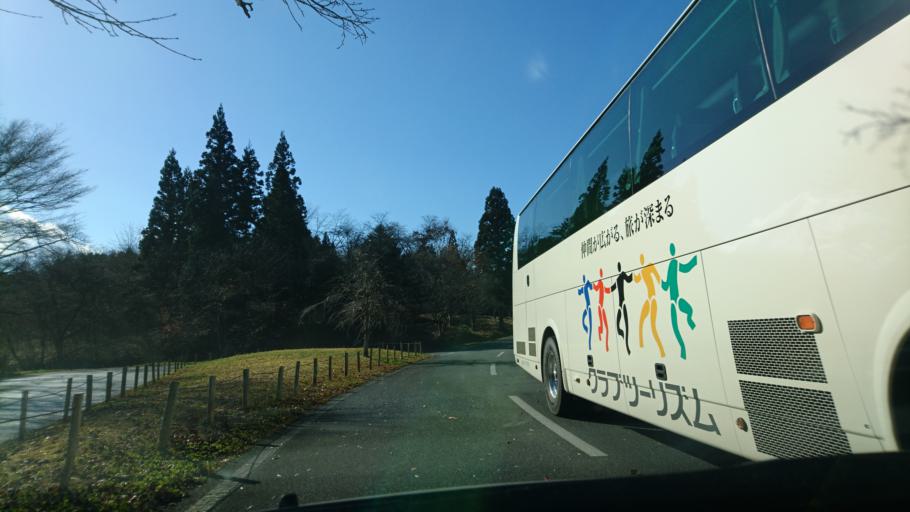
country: JP
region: Iwate
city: Ichinoseki
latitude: 38.9971
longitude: 141.0969
